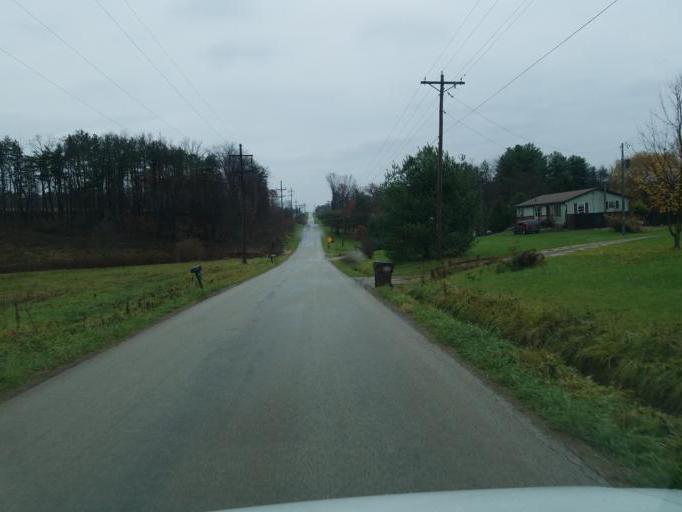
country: US
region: Ohio
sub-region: Sandusky County
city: Bellville
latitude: 40.5973
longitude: -82.5480
